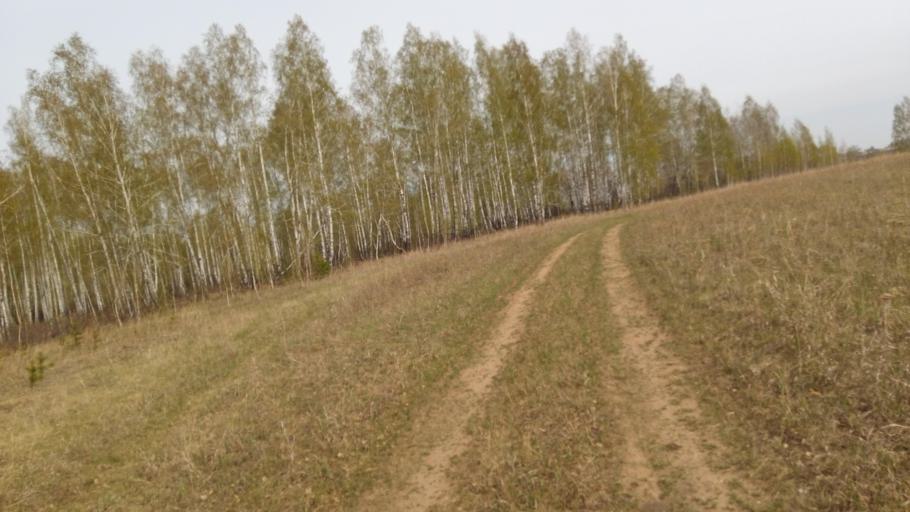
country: RU
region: Chelyabinsk
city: Timiryazevskiy
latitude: 55.0224
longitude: 60.8588
